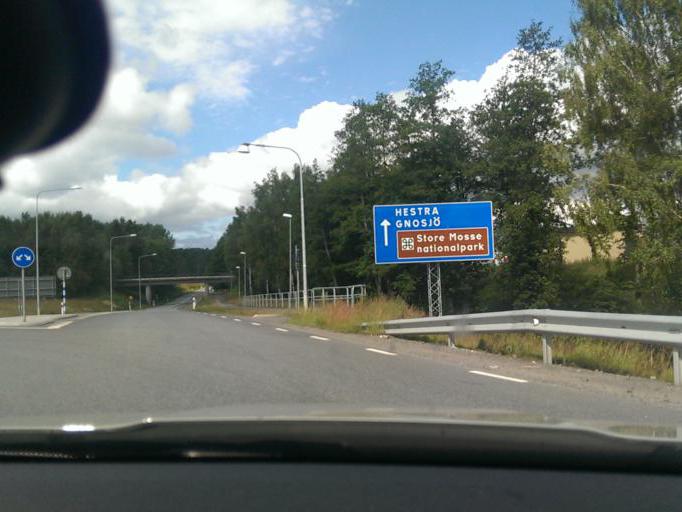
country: SE
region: Joenkoeping
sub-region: Varnamo Kommun
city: Varnamo
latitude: 57.2065
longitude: 14.0372
